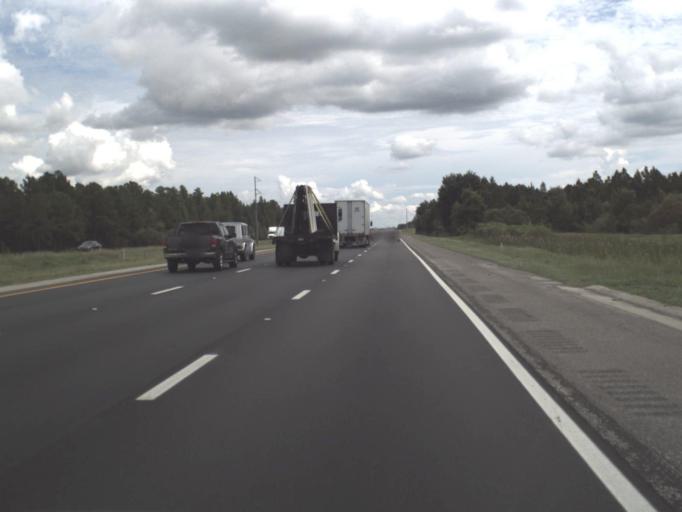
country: US
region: Florida
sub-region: Polk County
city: Lake Alfred
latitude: 28.1983
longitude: -81.7043
